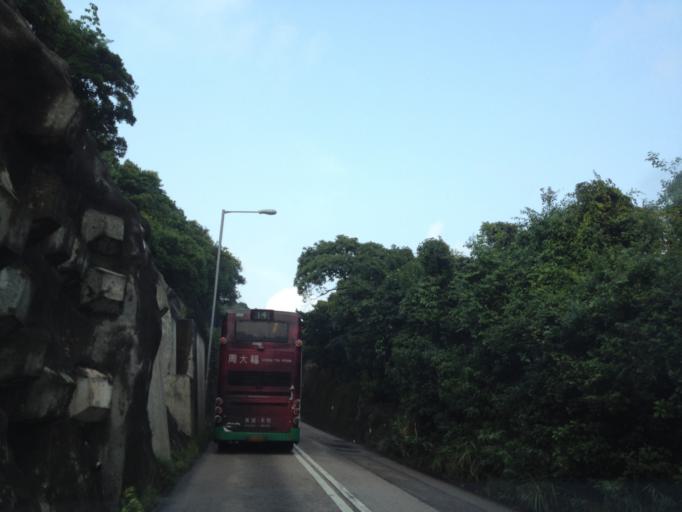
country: HK
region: Wanchai
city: Wan Chai
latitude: 22.2496
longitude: 114.2237
